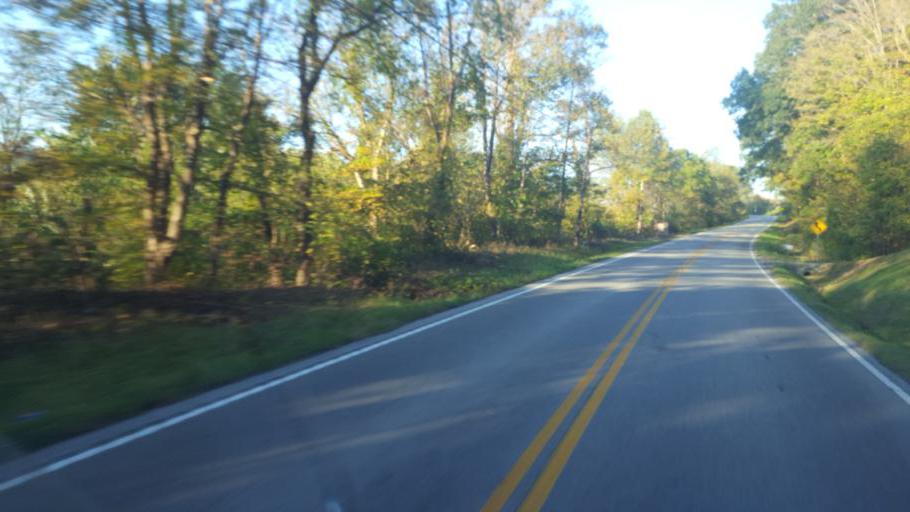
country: US
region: Ohio
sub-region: Scioto County
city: Portsmouth
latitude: 38.6916
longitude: -83.0504
